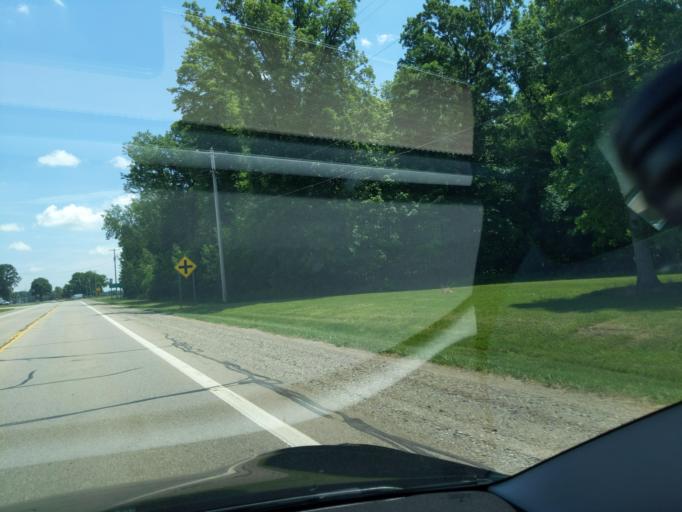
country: US
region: Michigan
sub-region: Clinton County
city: Fowler
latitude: 42.9947
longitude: -84.8518
